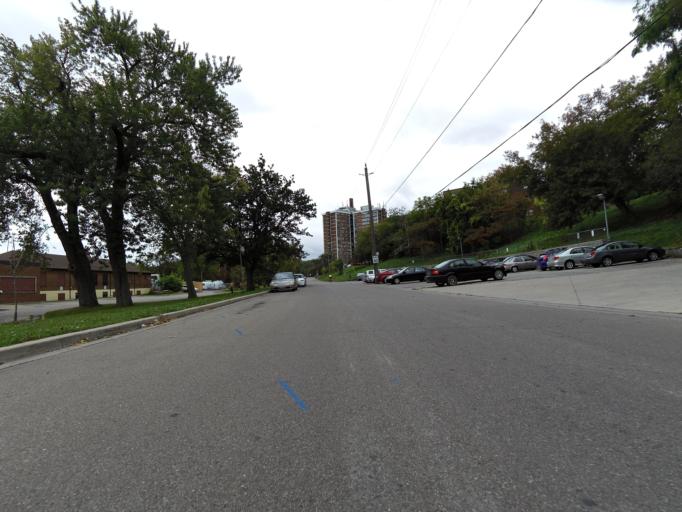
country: CA
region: Ontario
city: Scarborough
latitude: 43.7001
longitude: -79.2518
